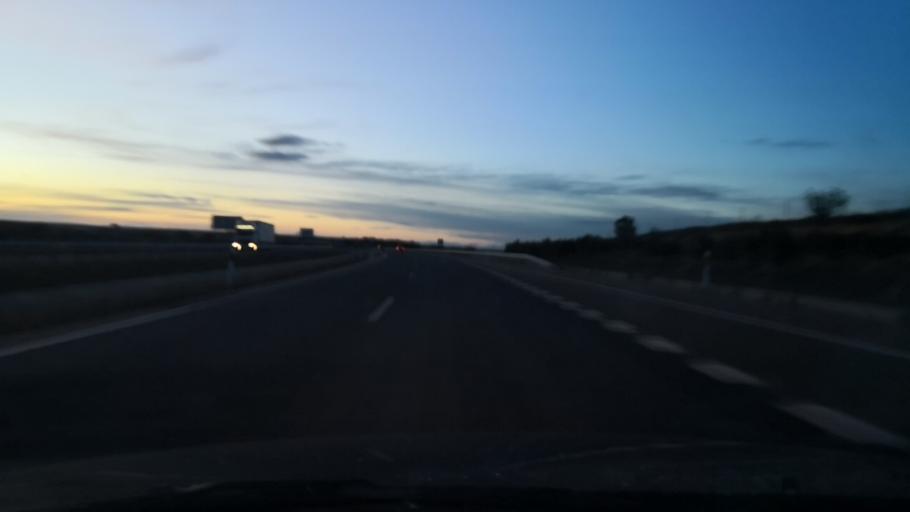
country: ES
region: Castille and Leon
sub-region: Provincia de Zamora
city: Toro
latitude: 41.5467
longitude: -5.3822
